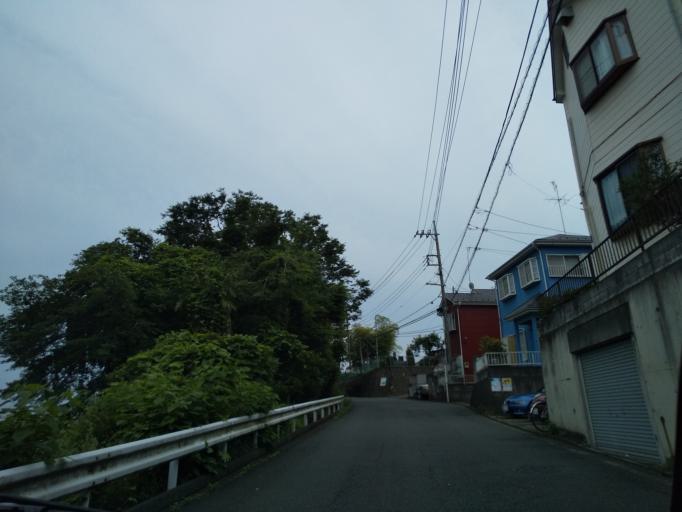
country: JP
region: Kanagawa
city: Atsugi
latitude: 35.4758
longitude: 139.3518
